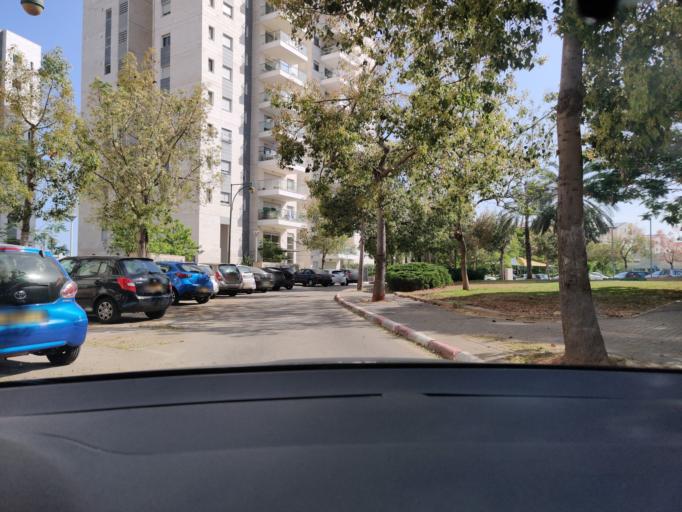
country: IL
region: Haifa
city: Hadera
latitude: 32.4673
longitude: 34.9537
